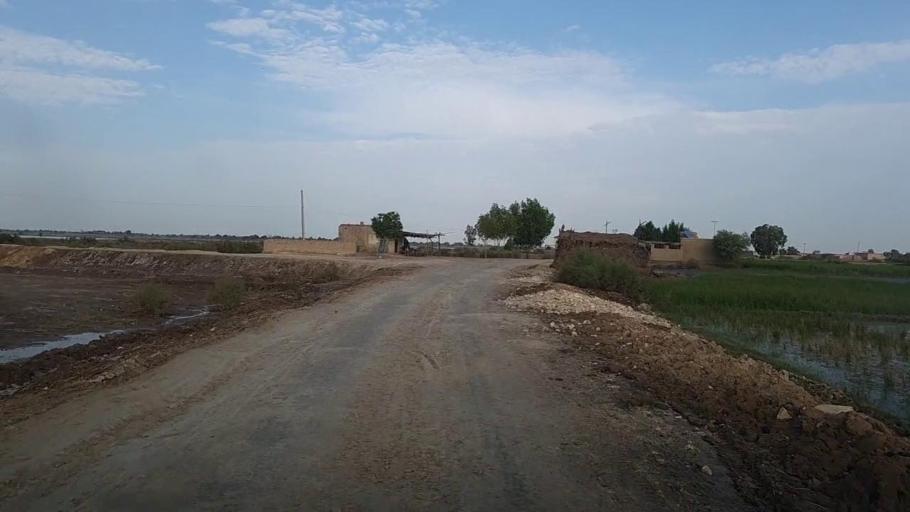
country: PK
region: Sindh
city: Thul
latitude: 28.2635
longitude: 68.8662
